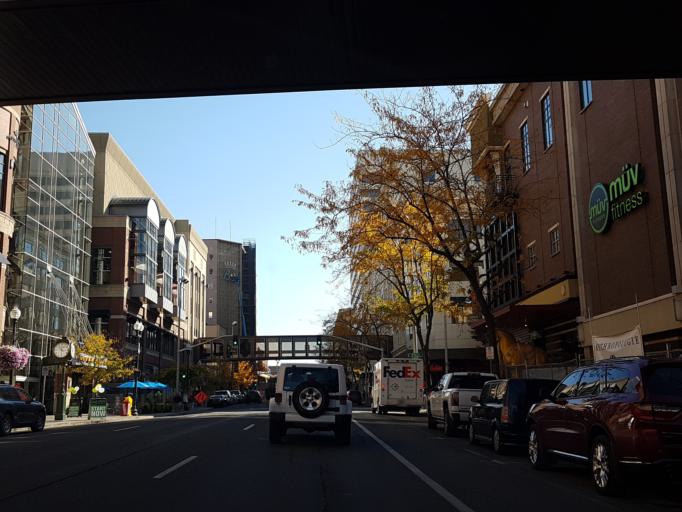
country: US
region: Washington
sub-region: Spokane County
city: Spokane
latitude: 47.6590
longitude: -117.4244
